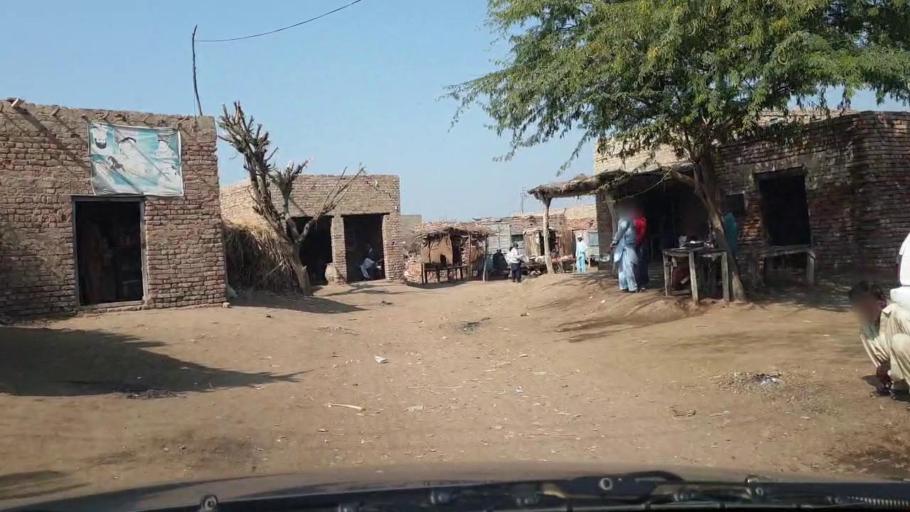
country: PK
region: Sindh
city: Jhol
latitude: 25.9048
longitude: 68.9973
